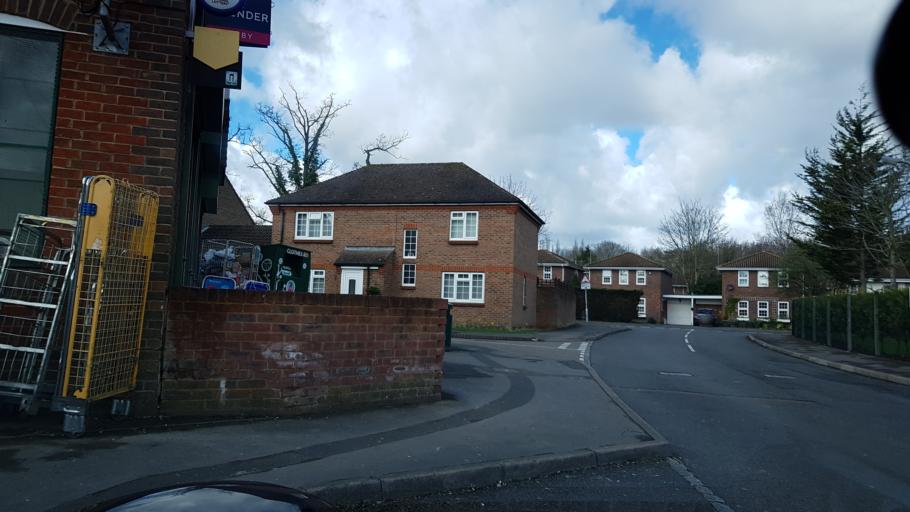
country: GB
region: England
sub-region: Surrey
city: Guildford
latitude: 51.2645
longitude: -0.5939
